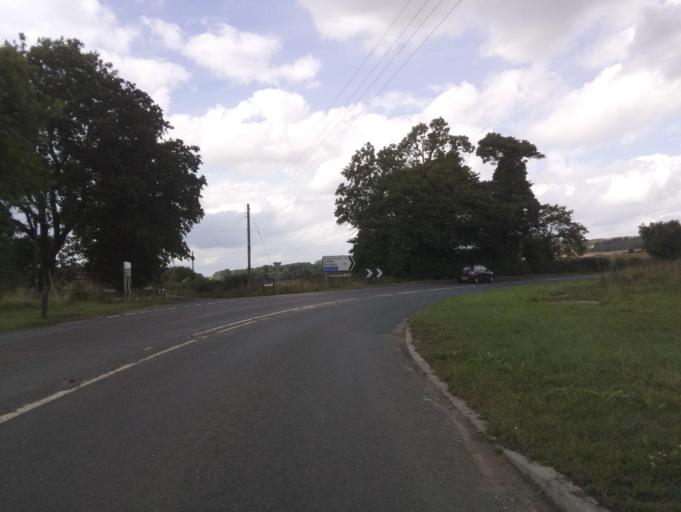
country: GB
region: England
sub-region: North Yorkshire
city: Catterick Garrison
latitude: 54.4250
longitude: -1.6835
